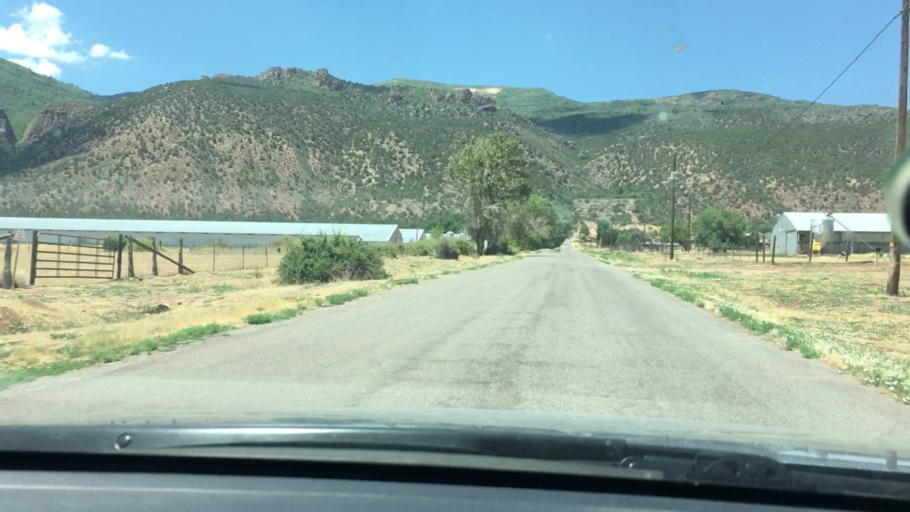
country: US
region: Utah
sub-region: Sanpete County
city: Moroni
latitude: 39.5422
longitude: -111.6433
